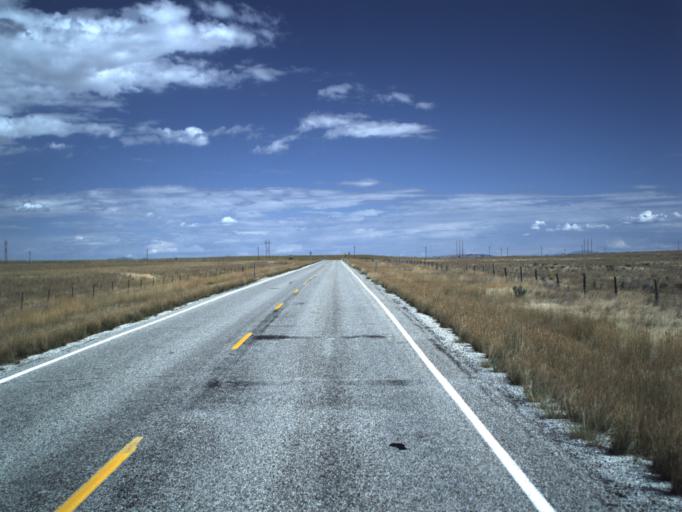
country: US
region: Idaho
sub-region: Oneida County
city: Malad City
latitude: 41.9601
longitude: -113.0667
